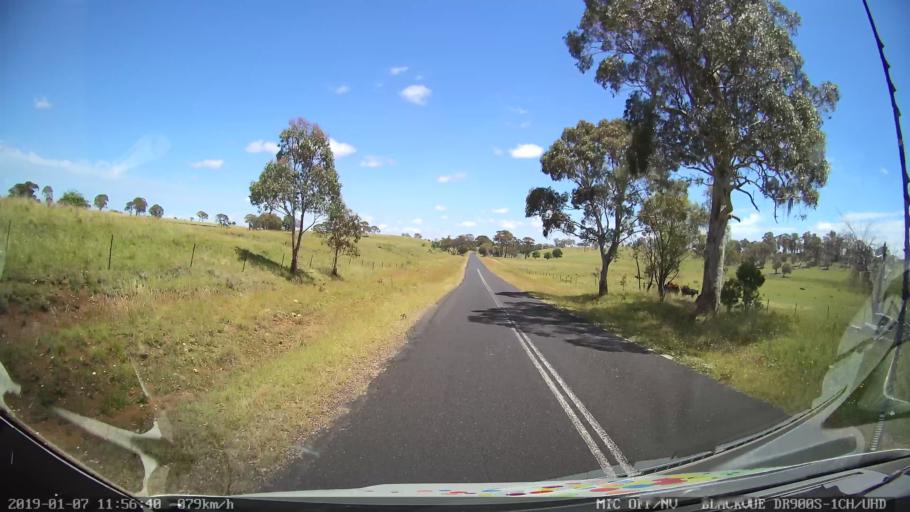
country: AU
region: New South Wales
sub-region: Guyra
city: Guyra
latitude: -30.2721
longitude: 151.6720
